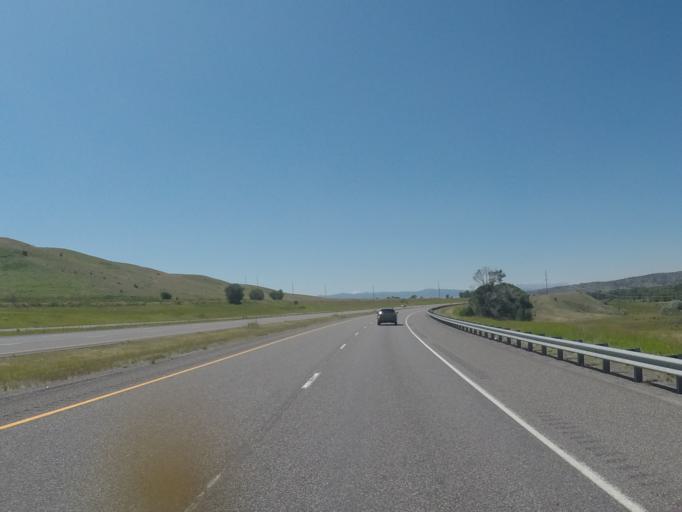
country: US
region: Montana
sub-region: Park County
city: Livingston
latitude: 45.7075
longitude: -110.3813
